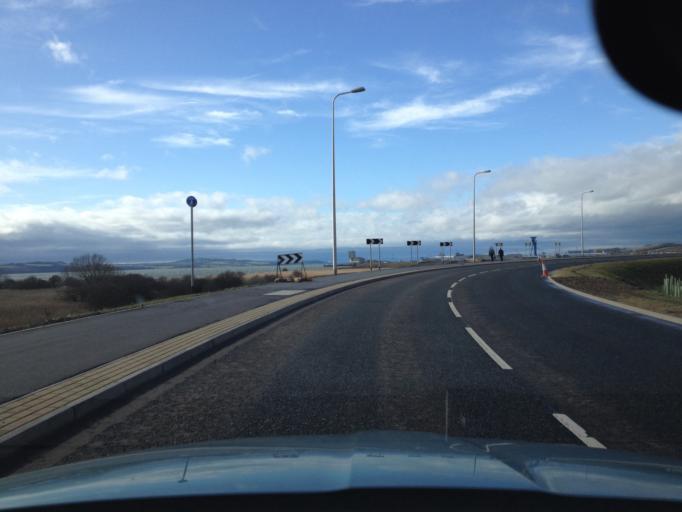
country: GB
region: Scotland
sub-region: Fife
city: Inverkeithing
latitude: 56.0184
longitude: -3.4099
